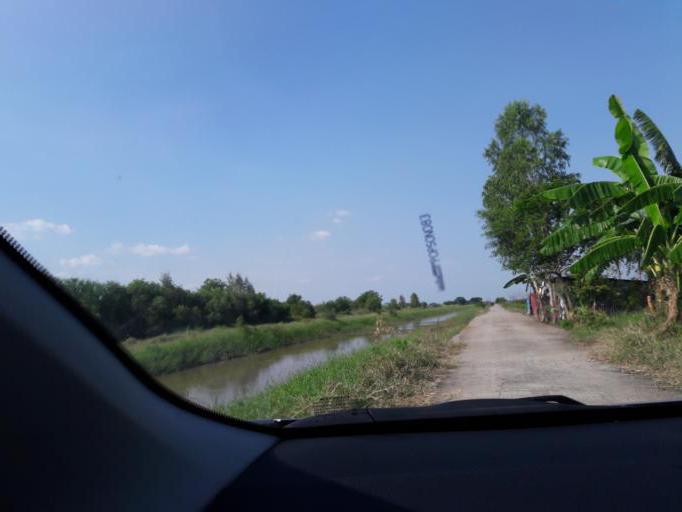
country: TH
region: Ang Thong
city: Ang Thong
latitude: 14.5479
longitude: 100.4068
